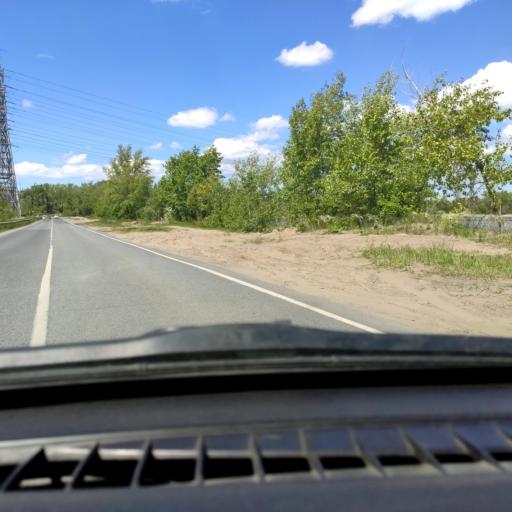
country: RU
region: Samara
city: Zhigulevsk
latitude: 53.4618
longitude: 49.5082
